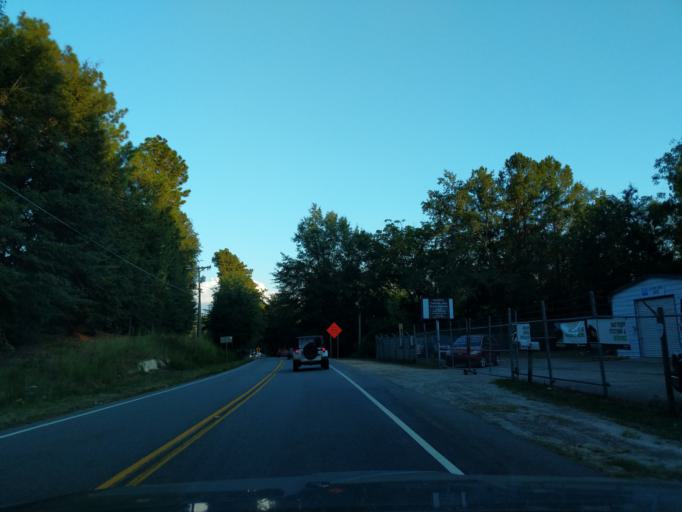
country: US
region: South Carolina
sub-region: Aiken County
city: Burnettown
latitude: 33.5272
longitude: -81.8535
